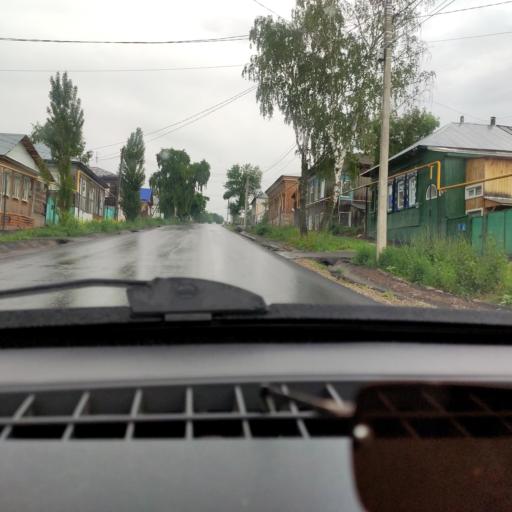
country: RU
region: Bashkortostan
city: Birsk
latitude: 55.4215
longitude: 55.5249
